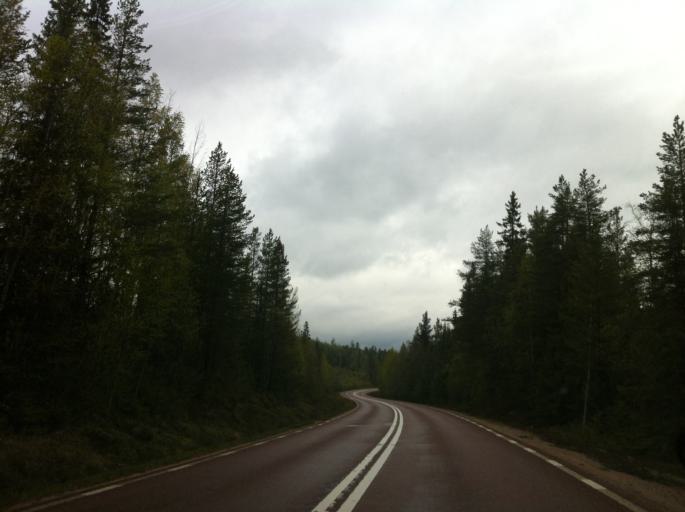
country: SE
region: Jaemtland
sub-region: Harjedalens Kommun
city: Sveg
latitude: 61.8715
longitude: 14.6315
